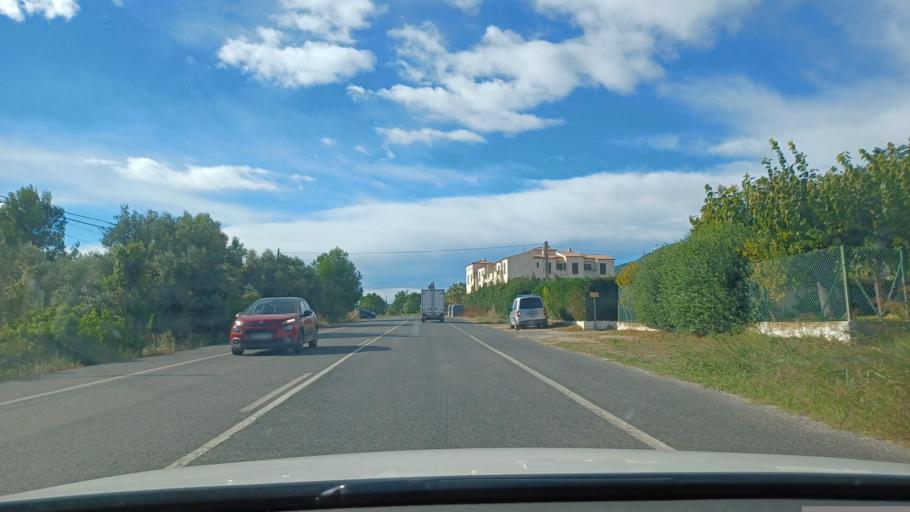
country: ES
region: Catalonia
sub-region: Provincia de Tarragona
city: Sant Carles de la Rapita
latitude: 40.5867
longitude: 0.5592
